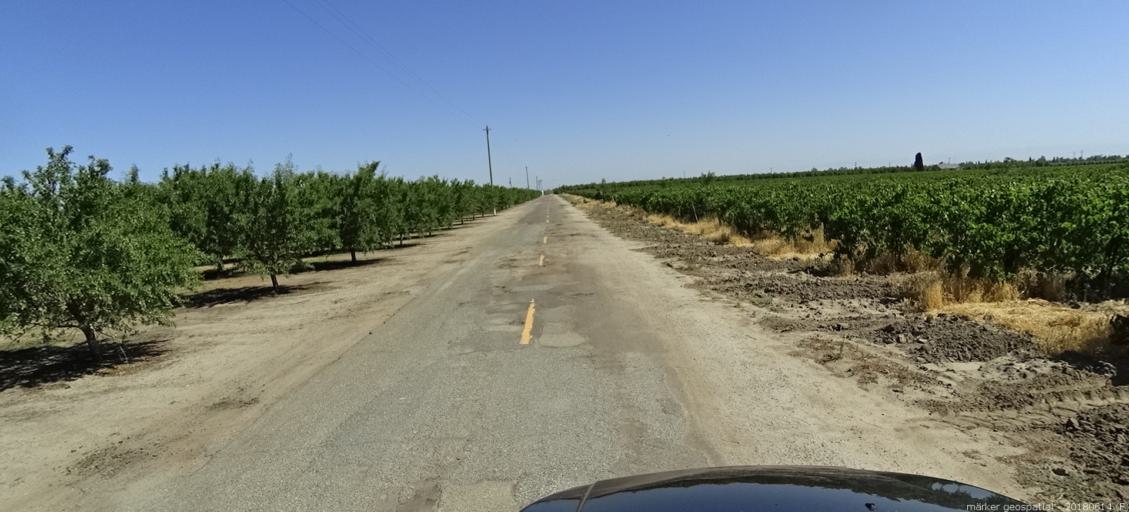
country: US
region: California
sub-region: Madera County
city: Madera
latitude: 36.9785
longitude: -120.1379
